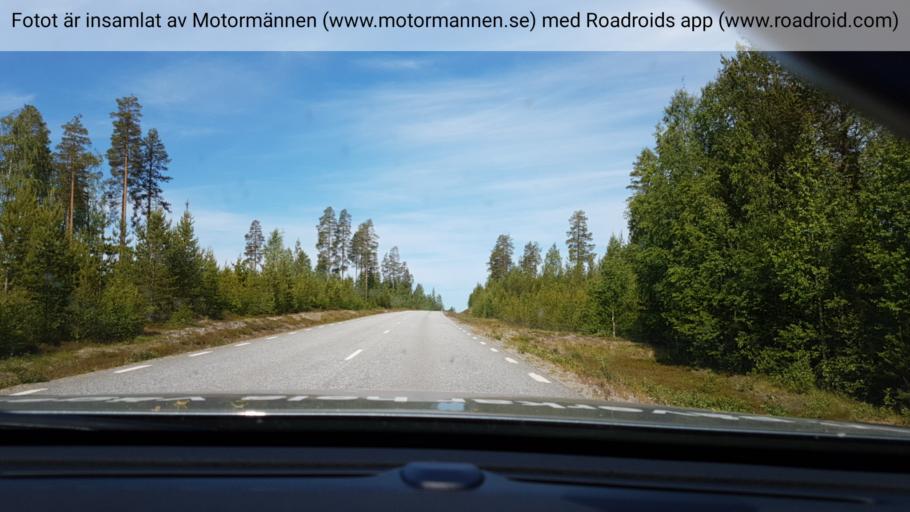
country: SE
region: Vaesterbotten
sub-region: Dorotea Kommun
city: Dorotea
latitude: 64.2218
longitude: 16.8648
